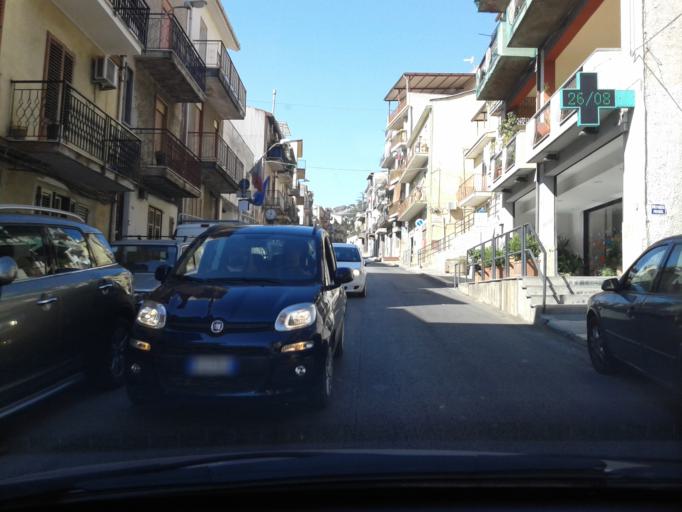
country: IT
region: Sicily
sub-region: Palermo
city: Pioppo
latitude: 38.0480
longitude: 13.2295
